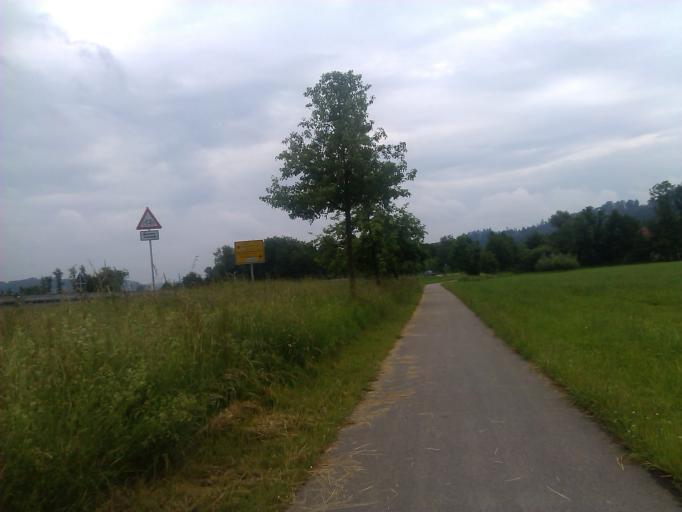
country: DE
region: Baden-Wuerttemberg
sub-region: Regierungsbezirk Stuttgart
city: Oberrot
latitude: 49.0212
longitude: 9.6602
